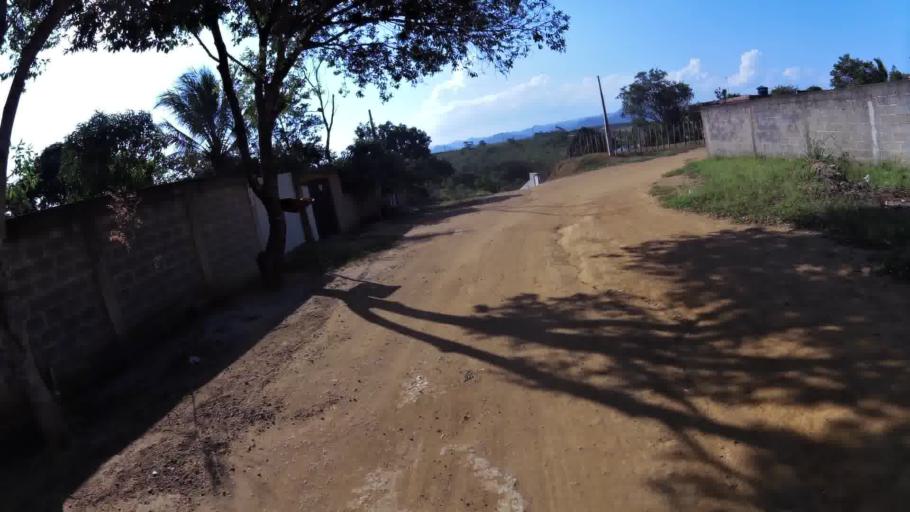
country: BR
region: Espirito Santo
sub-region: Guarapari
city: Guarapari
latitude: -20.7193
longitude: -40.5323
